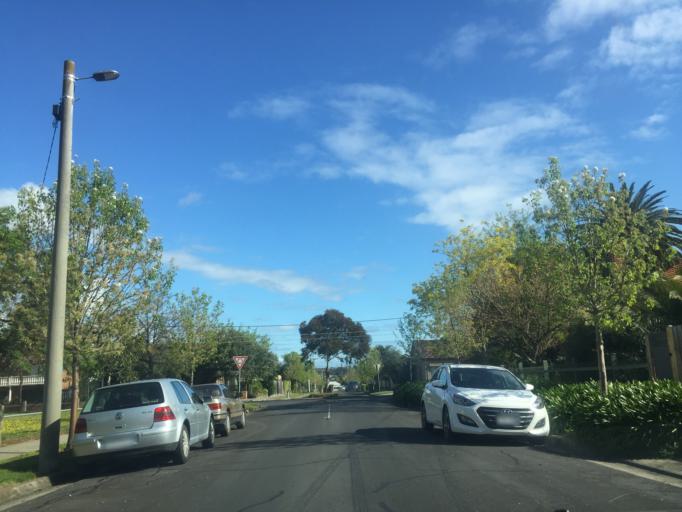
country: AU
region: Victoria
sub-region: Darebin
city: Reservoir
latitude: -37.7277
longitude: 145.0081
